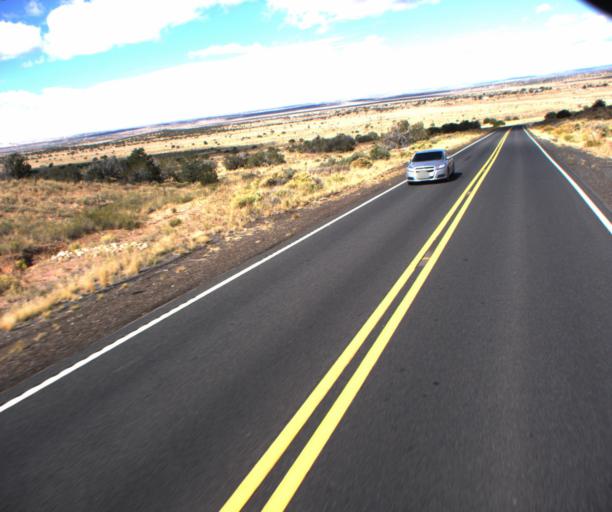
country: US
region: Arizona
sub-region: Apache County
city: Houck
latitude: 35.0345
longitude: -109.2618
